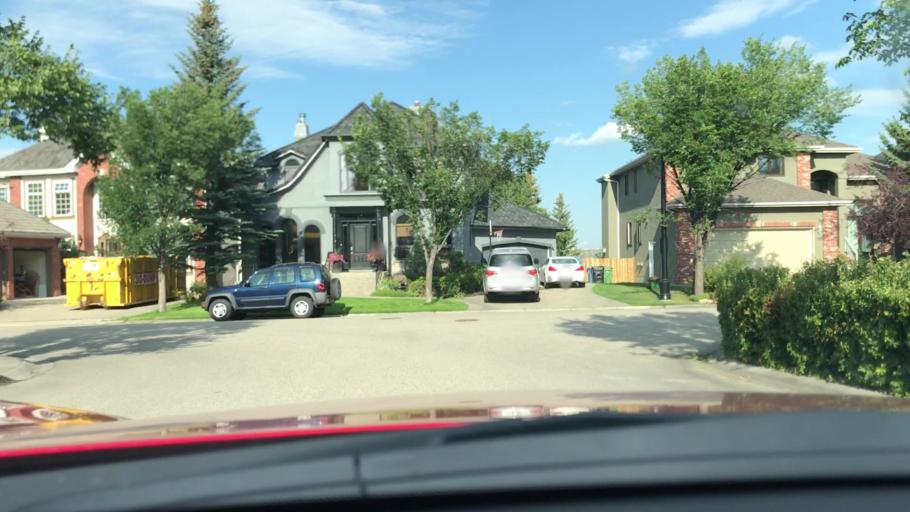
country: CA
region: Alberta
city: Calgary
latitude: 51.0245
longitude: -114.1745
